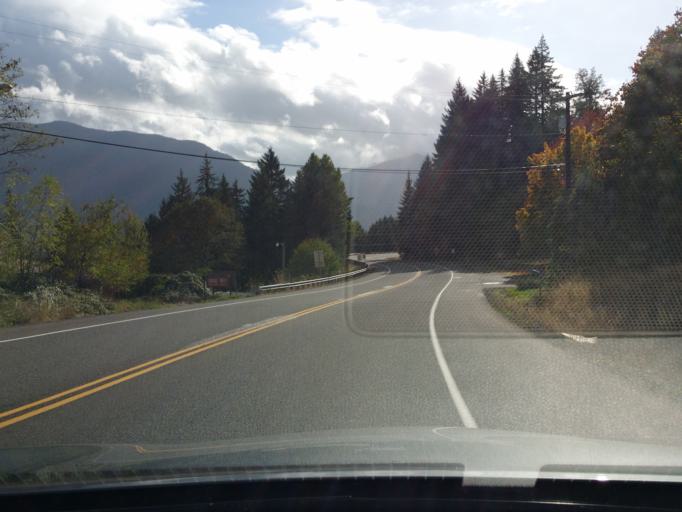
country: US
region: Washington
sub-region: Skamania County
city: Carson
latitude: 45.7224
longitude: -121.8202
